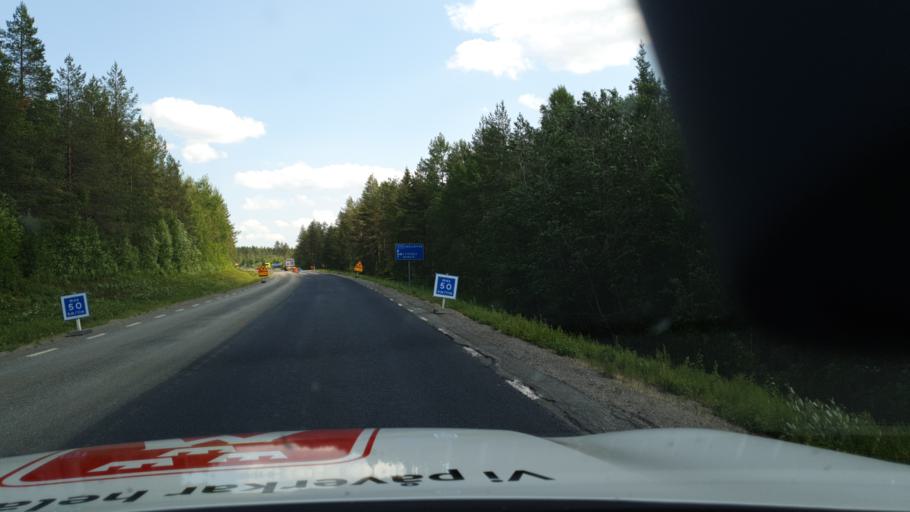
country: SE
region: Vaesterbotten
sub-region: Norsjo Kommun
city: Norsjoe
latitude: 64.9923
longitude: 19.2918
